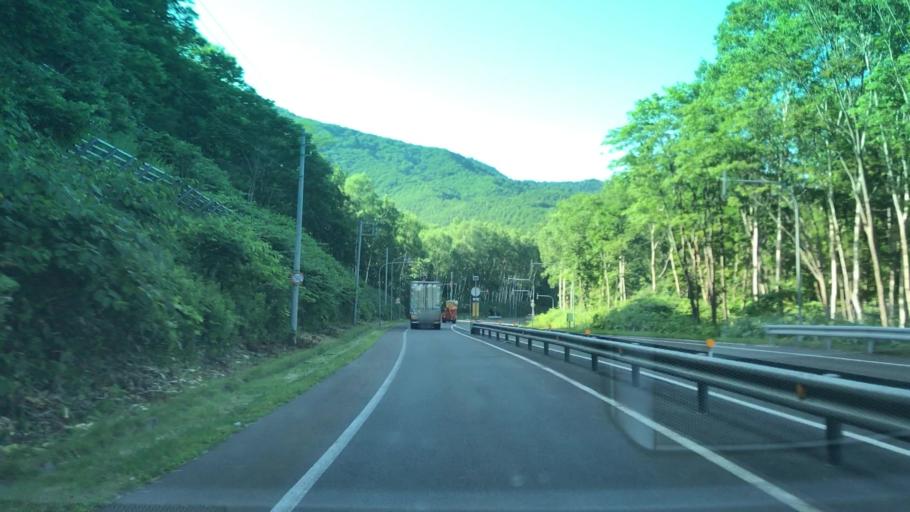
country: JP
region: Hokkaido
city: Yoichi
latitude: 43.0690
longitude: 140.6999
